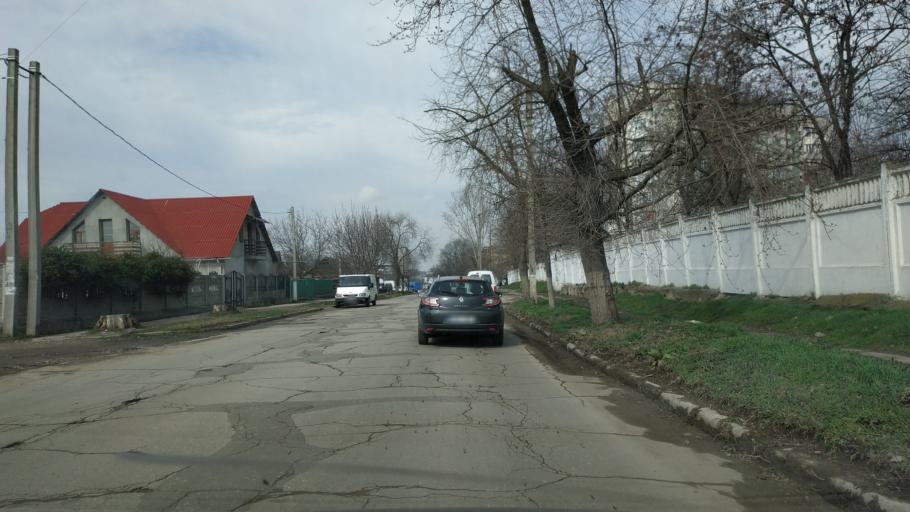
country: MD
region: Cahul
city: Cahul
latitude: 45.8940
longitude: 28.2002
